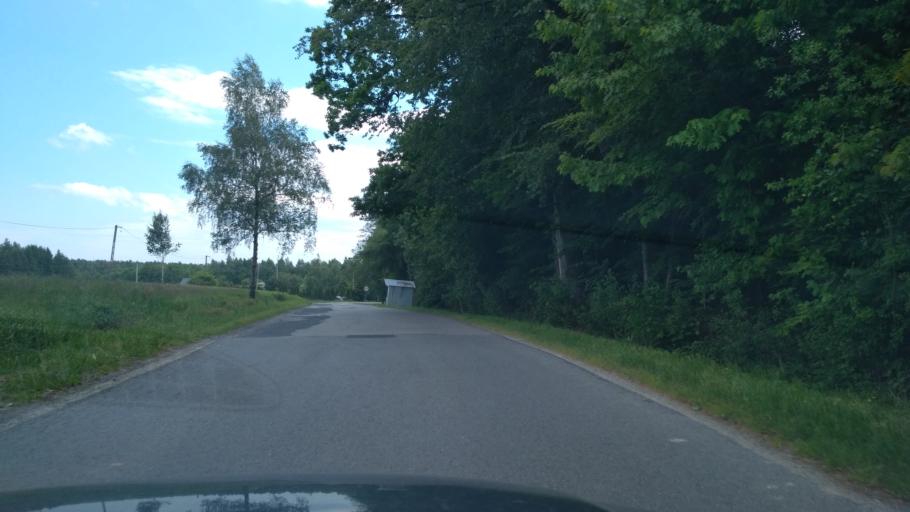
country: PL
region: Subcarpathian Voivodeship
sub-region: Powiat ropczycko-sedziszowski
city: Ropczyce
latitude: 50.0163
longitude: 21.6093
